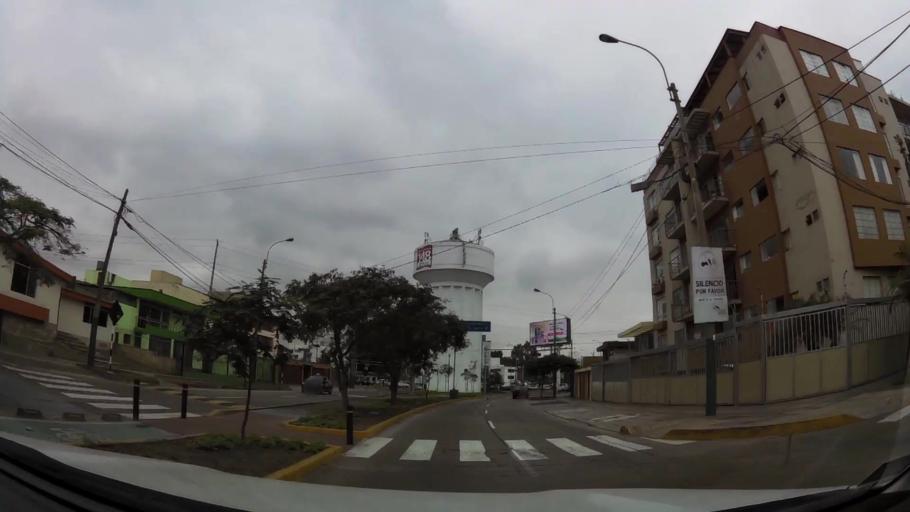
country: PE
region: Lima
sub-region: Lima
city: San Luis
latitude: -12.1094
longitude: -76.9801
